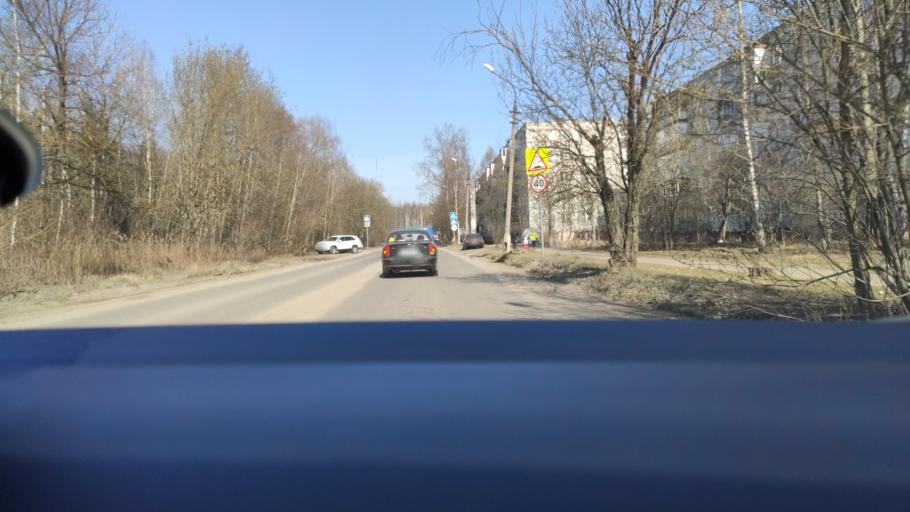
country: RU
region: Moskovskaya
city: Elektrostal'
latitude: 55.7674
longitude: 38.4175
